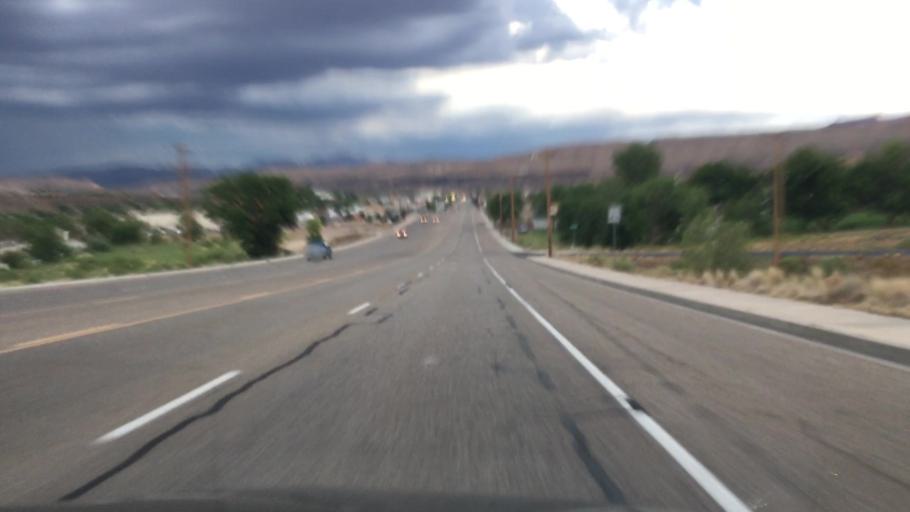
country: US
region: Utah
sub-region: Washington County
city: Hurricane
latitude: 37.1763
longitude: -113.3224
